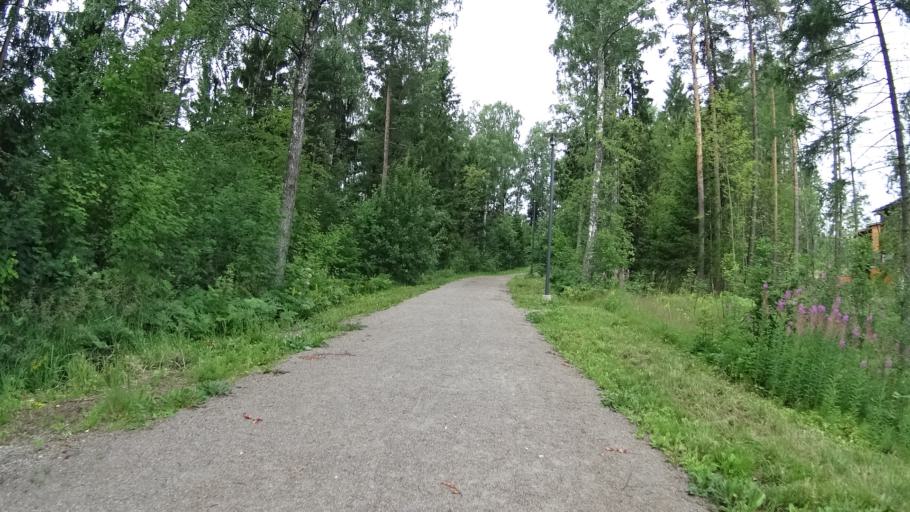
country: FI
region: Uusimaa
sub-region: Helsinki
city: Teekkarikylae
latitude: 60.2340
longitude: 24.8281
